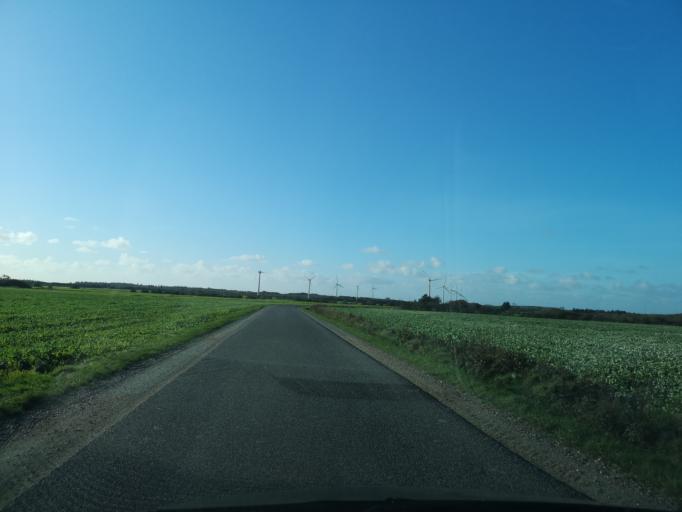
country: DK
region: Central Jutland
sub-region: Ringkobing-Skjern Kommune
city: Tarm
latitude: 55.8035
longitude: 8.4557
